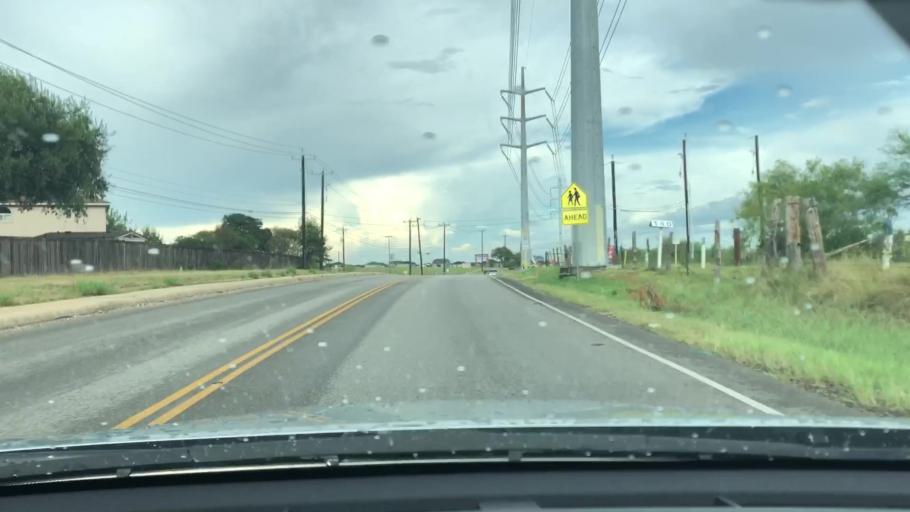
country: US
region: Texas
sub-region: Bexar County
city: Converse
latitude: 29.4727
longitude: -98.3349
